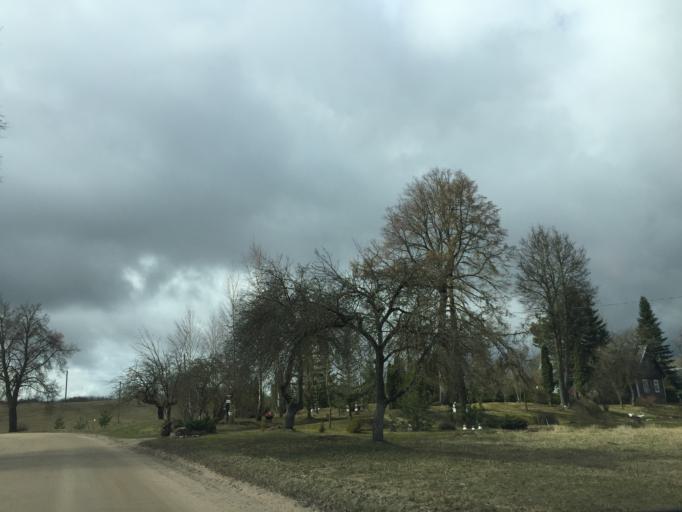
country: LV
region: Ilukste
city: Ilukste
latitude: 56.0697
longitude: 26.1215
